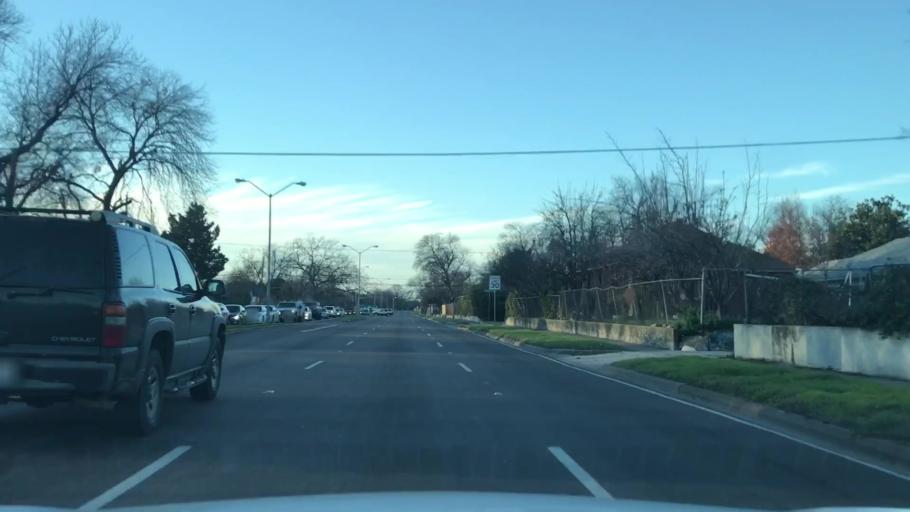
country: US
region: Texas
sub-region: Dallas County
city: Dallas
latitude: 32.7918
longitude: -96.7569
